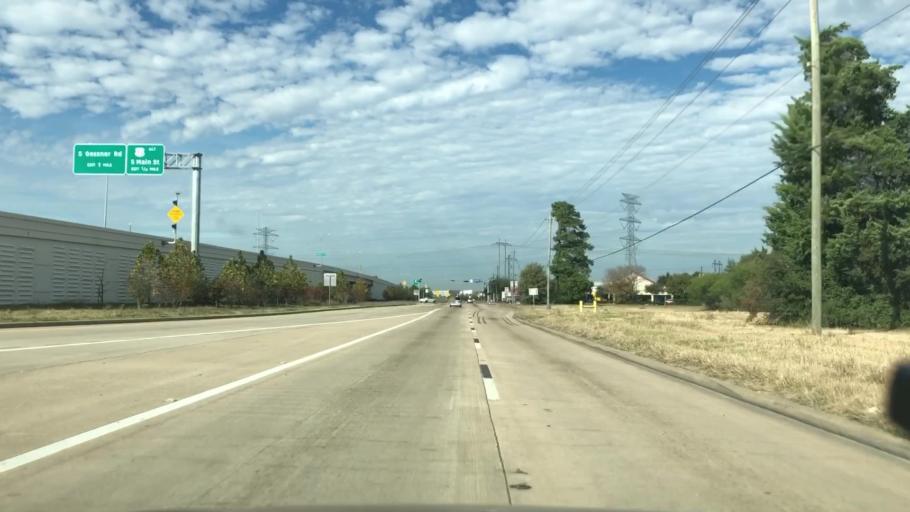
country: US
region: Texas
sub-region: Fort Bend County
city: Missouri City
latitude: 29.6203
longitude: -95.5063
